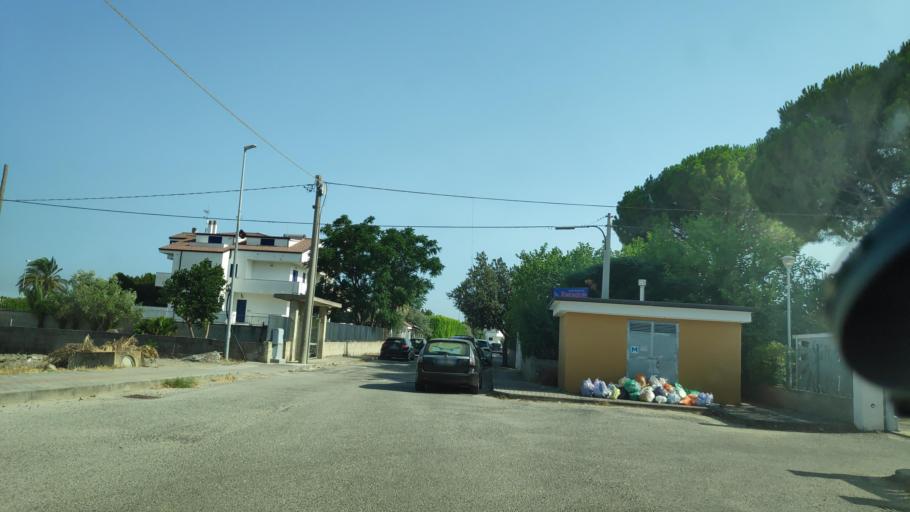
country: IT
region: Calabria
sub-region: Provincia di Catanzaro
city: Isca Marina
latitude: 38.6015
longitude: 16.5643
